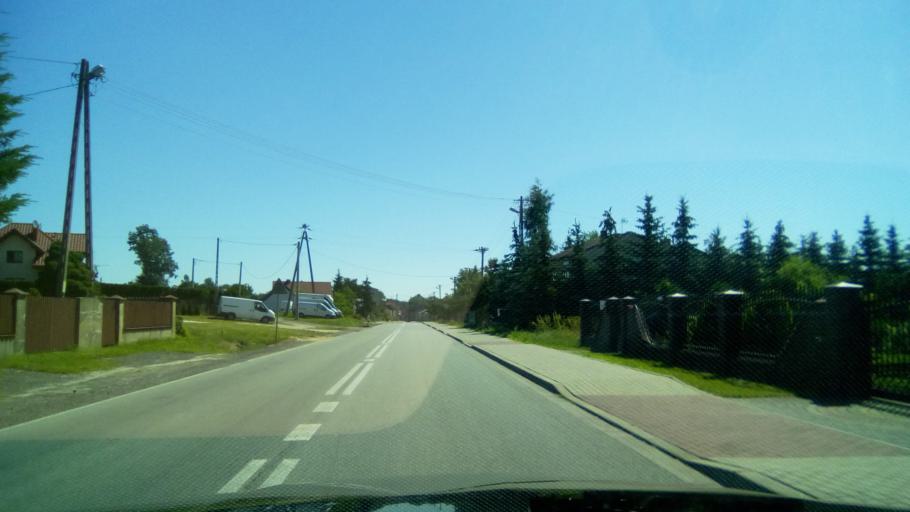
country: PL
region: Masovian Voivodeship
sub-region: Powiat przysuski
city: Odrzywol
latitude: 51.5181
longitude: 20.5477
